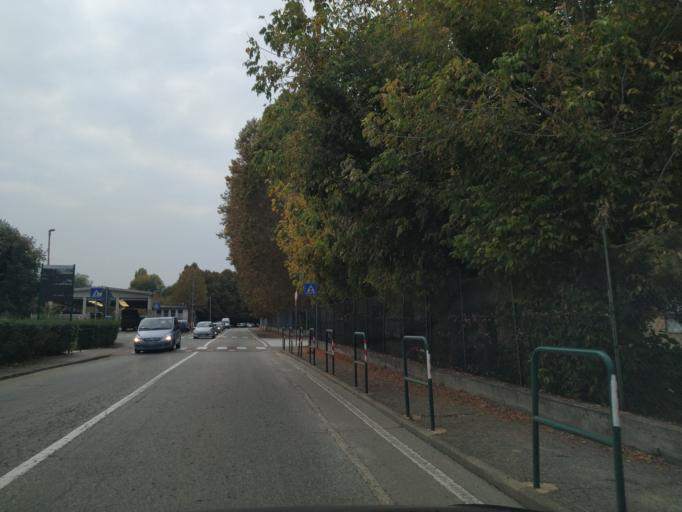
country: IT
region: Piedmont
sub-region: Provincia di Torino
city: Chivasso
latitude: 45.1853
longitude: 7.8889
